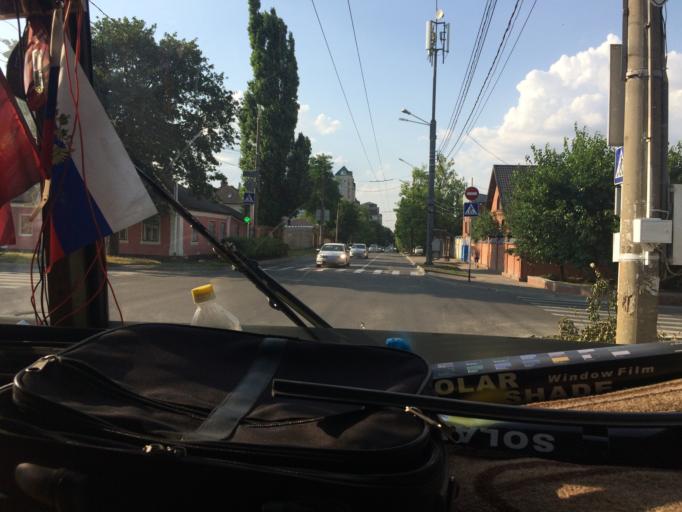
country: RU
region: Stavropol'skiy
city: Stavropol'
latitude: 45.0285
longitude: 41.9533
